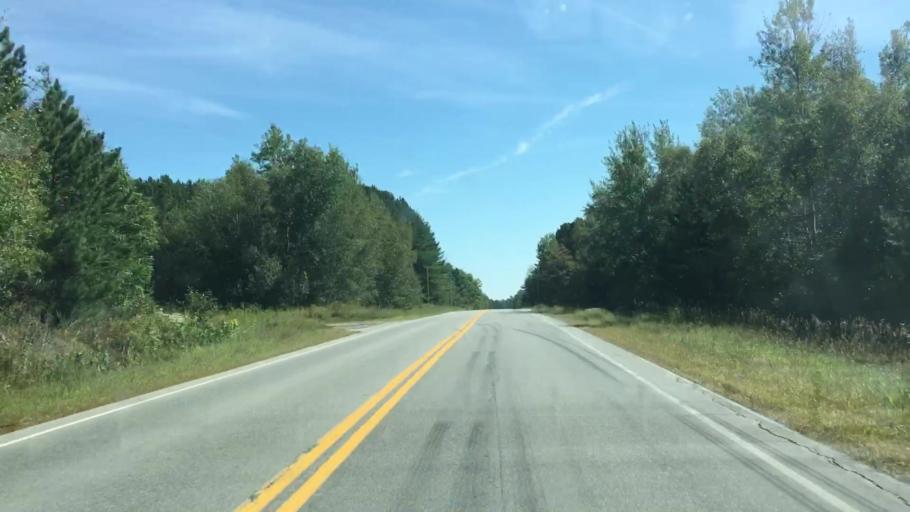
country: US
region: Maine
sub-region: Piscataquis County
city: Milo
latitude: 45.2281
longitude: -68.9327
